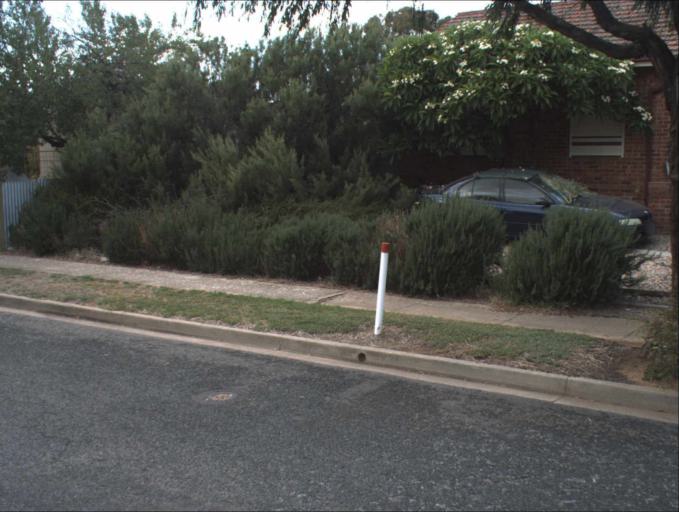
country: AU
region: South Australia
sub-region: Port Adelaide Enfield
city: Blair Athol
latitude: -34.8594
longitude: 138.5986
